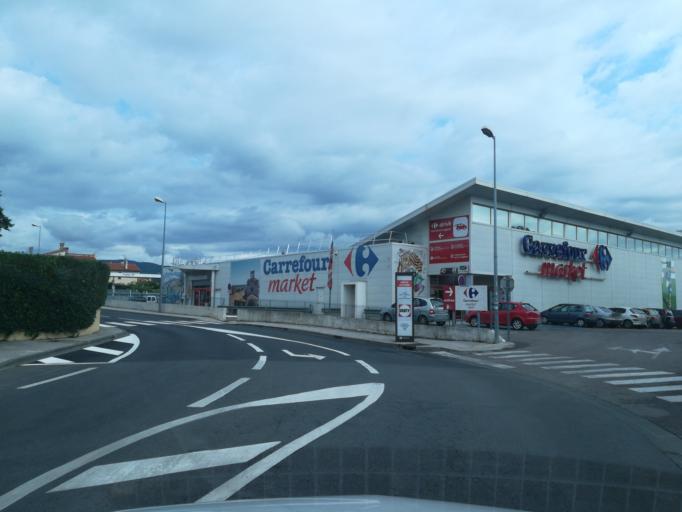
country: FR
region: Languedoc-Roussillon
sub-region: Departement des Pyrenees-Orientales
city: Ceret
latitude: 42.4899
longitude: 2.7521
